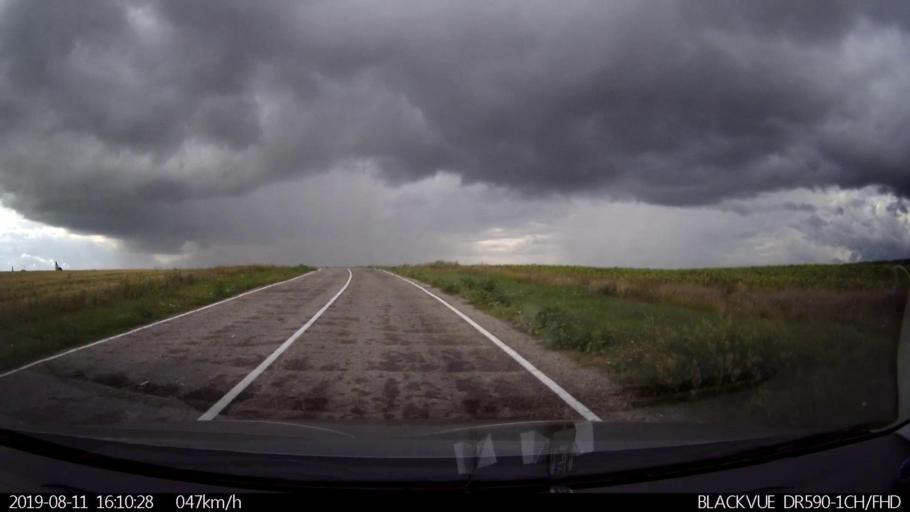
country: RU
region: Ulyanovsk
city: Ignatovka
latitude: 53.9988
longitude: 47.6547
